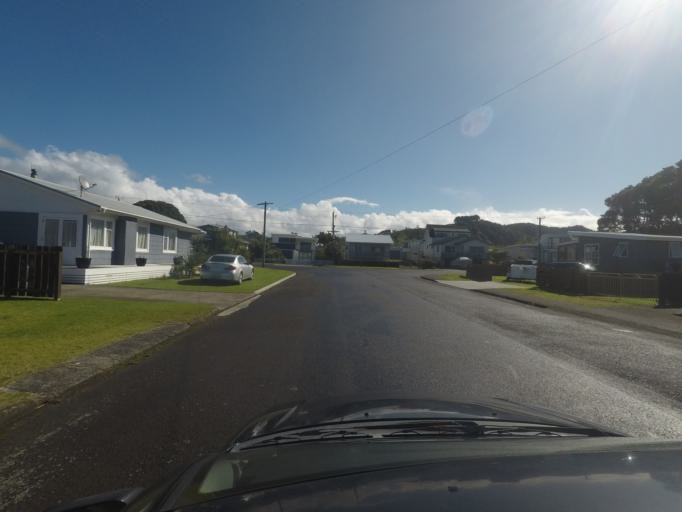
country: NZ
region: Bay of Plenty
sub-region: Western Bay of Plenty District
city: Waihi Beach
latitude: -37.4045
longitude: 175.9414
